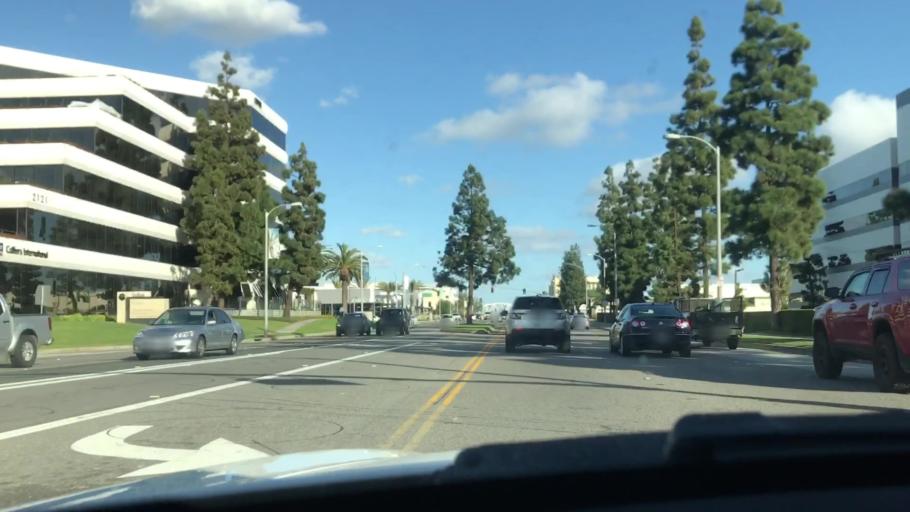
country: US
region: California
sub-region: Los Angeles County
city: Del Aire
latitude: 33.9019
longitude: -118.3883
